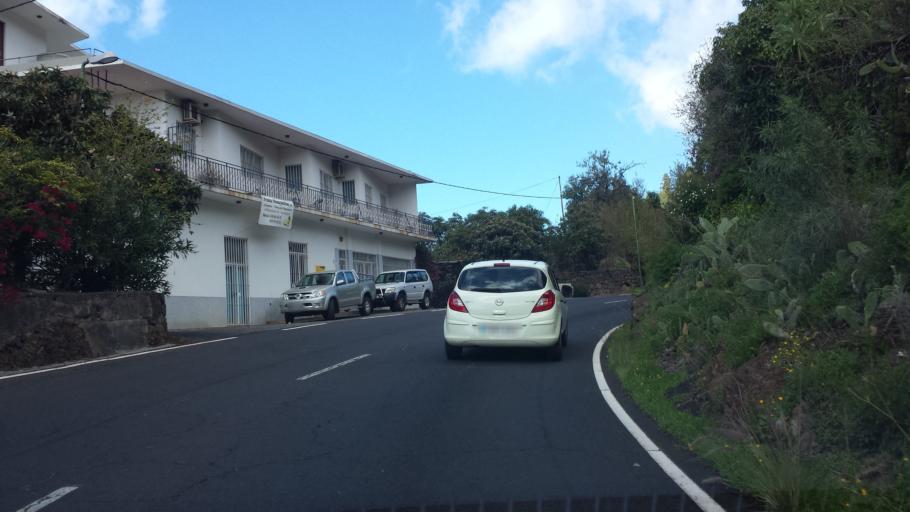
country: ES
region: Canary Islands
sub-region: Provincia de Santa Cruz de Tenerife
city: Tijarafe
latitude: 28.7233
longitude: -17.9589
